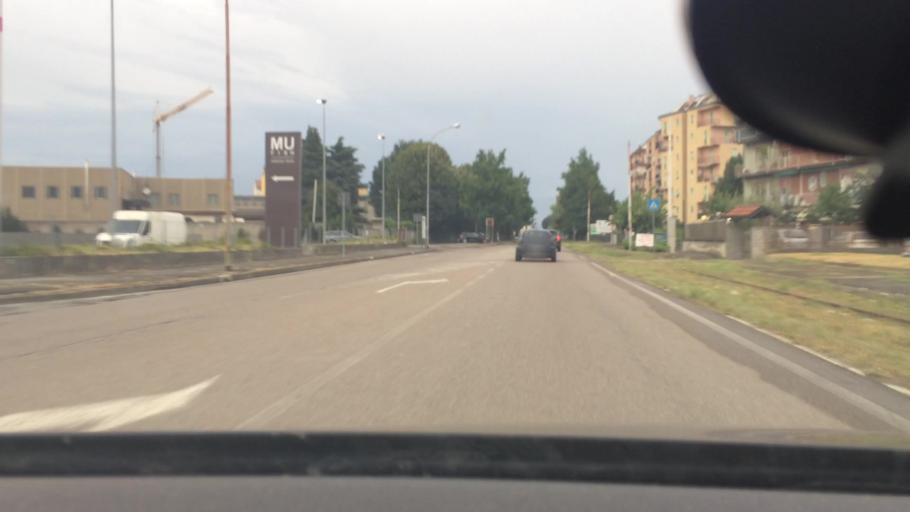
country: IT
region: Lombardy
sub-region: Provincia di Monza e Brianza
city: Nova Milanese
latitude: 45.5805
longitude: 9.1940
